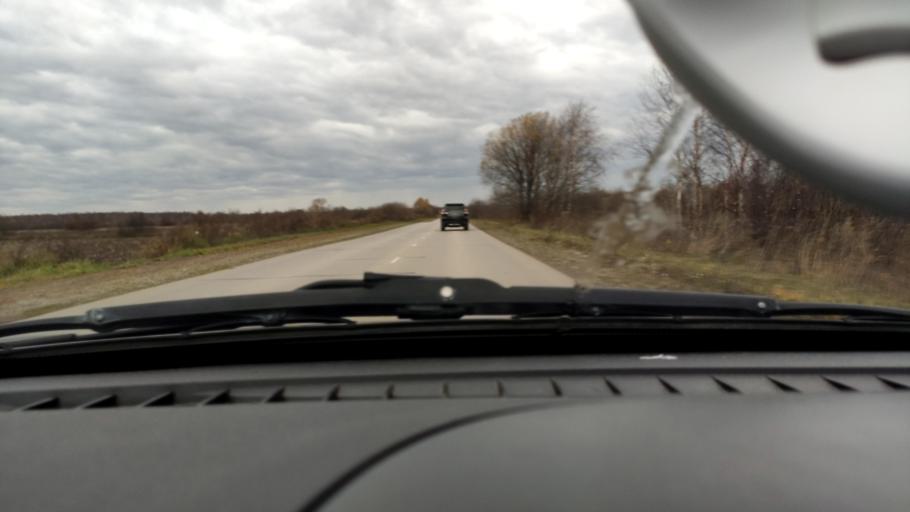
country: RU
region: Perm
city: Kondratovo
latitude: 57.9985
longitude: 56.0780
